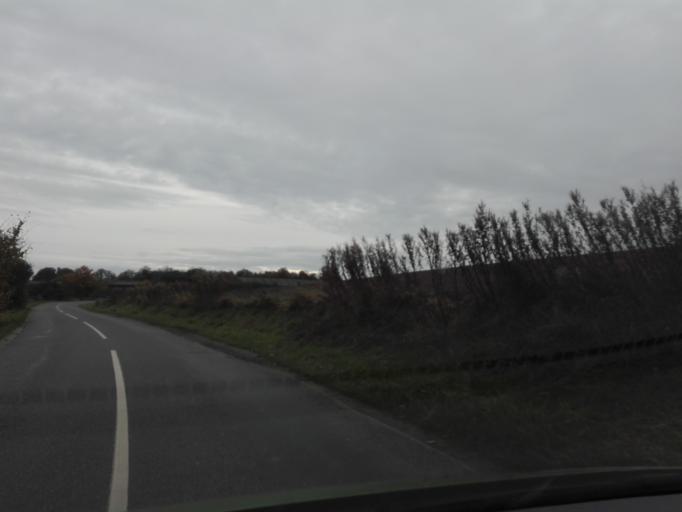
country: DK
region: Central Jutland
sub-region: Arhus Kommune
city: Solbjerg
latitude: 56.0635
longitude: 10.0874
